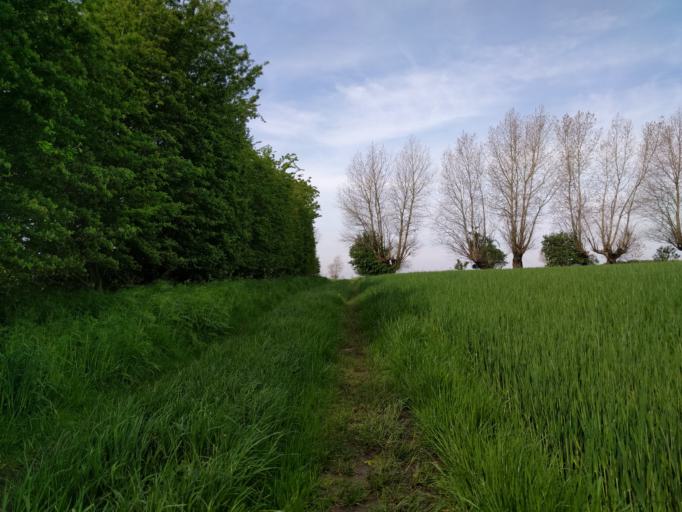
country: DK
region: South Denmark
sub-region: Odense Kommune
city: Bullerup
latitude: 55.3916
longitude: 10.5007
